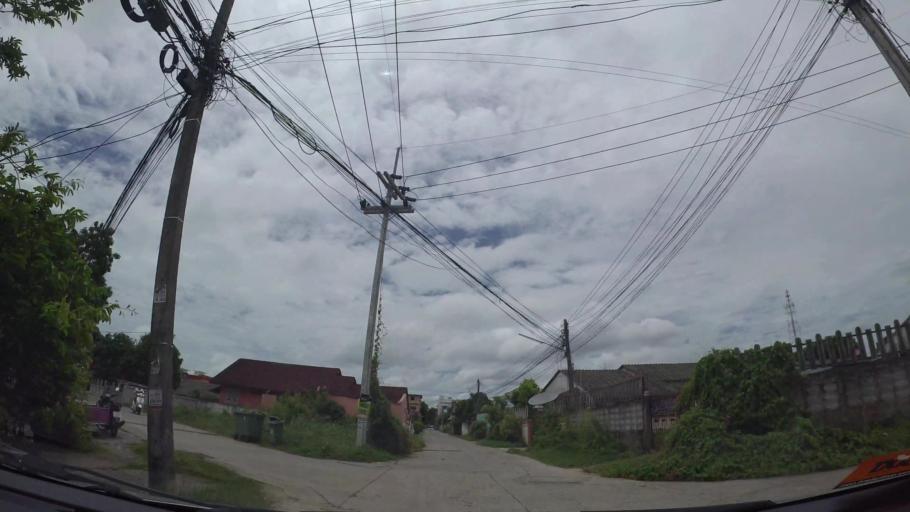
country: TH
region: Chon Buri
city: Sattahip
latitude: 12.7599
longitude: 100.8990
